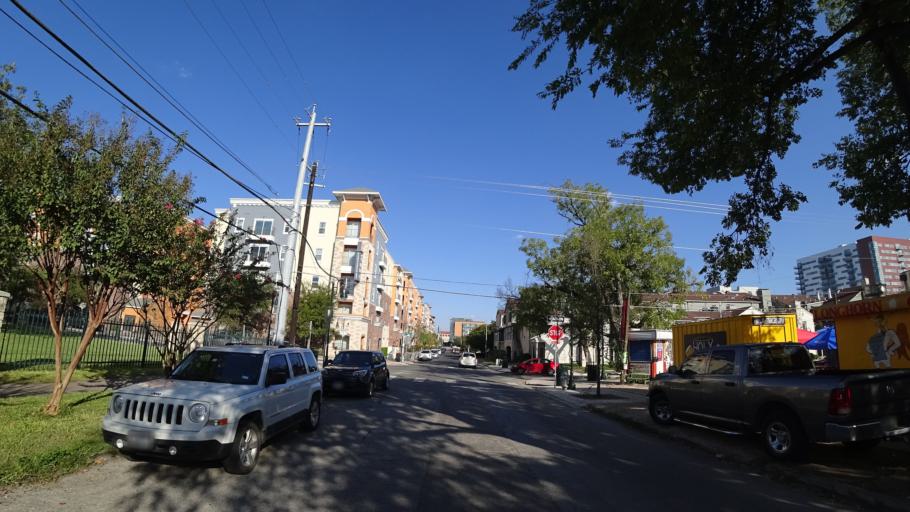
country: US
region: Texas
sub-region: Travis County
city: Austin
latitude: 30.2907
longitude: -97.7447
